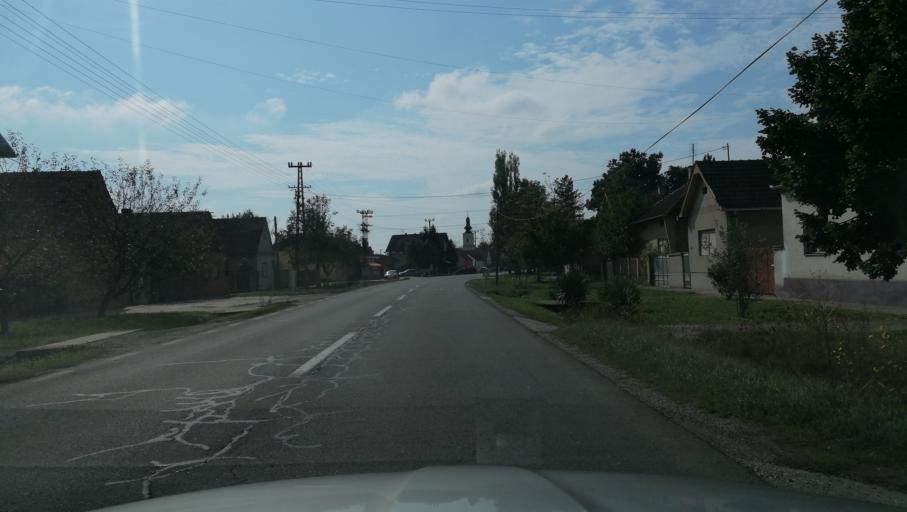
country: RS
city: Bosut
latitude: 44.9346
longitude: 19.3666
